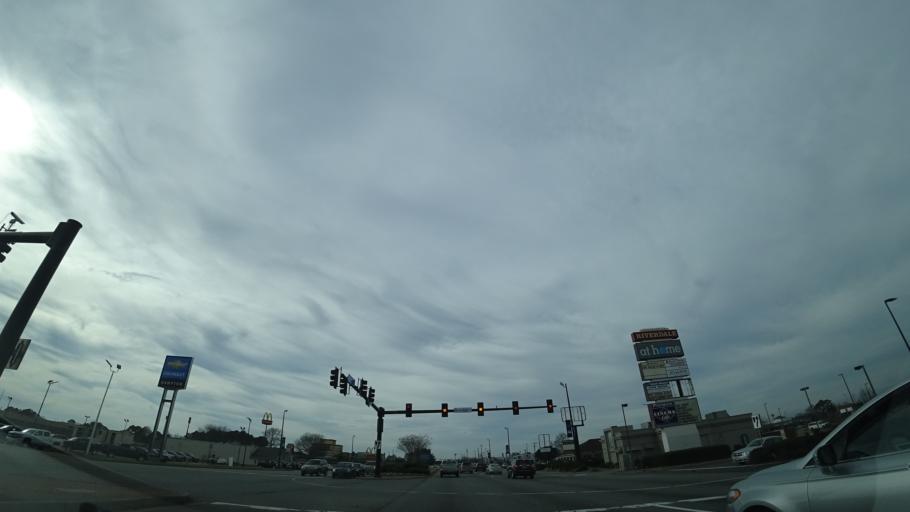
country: US
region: Virginia
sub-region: City of Hampton
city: Hampton
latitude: 37.0425
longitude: -76.3851
